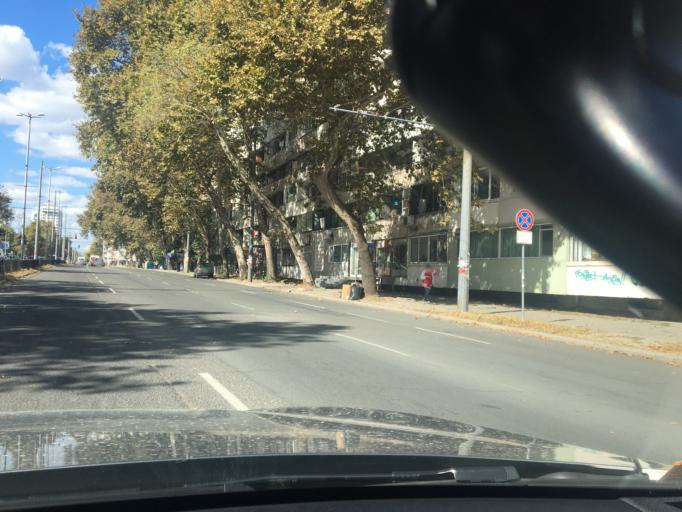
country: BG
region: Burgas
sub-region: Obshtina Burgas
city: Burgas
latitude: 42.5058
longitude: 27.4727
